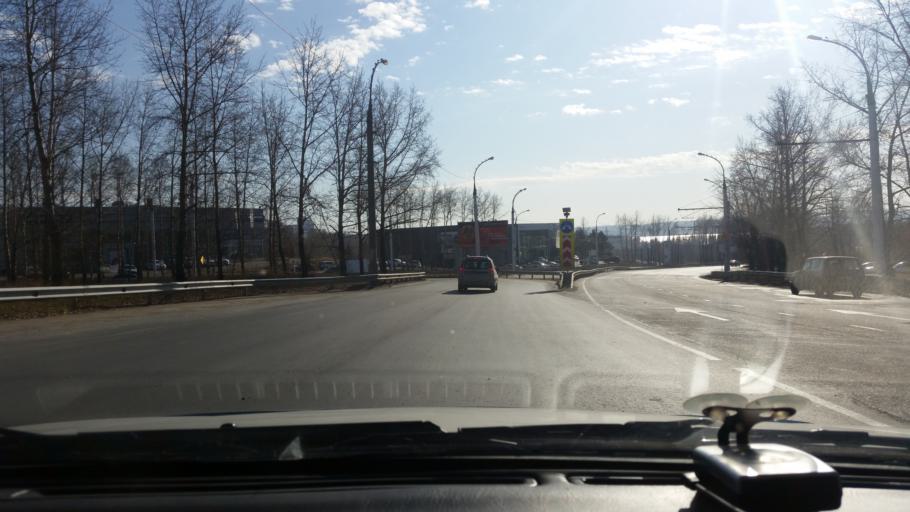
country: RU
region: Irkutsk
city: Dzerzhinsk
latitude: 52.2611
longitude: 104.3506
